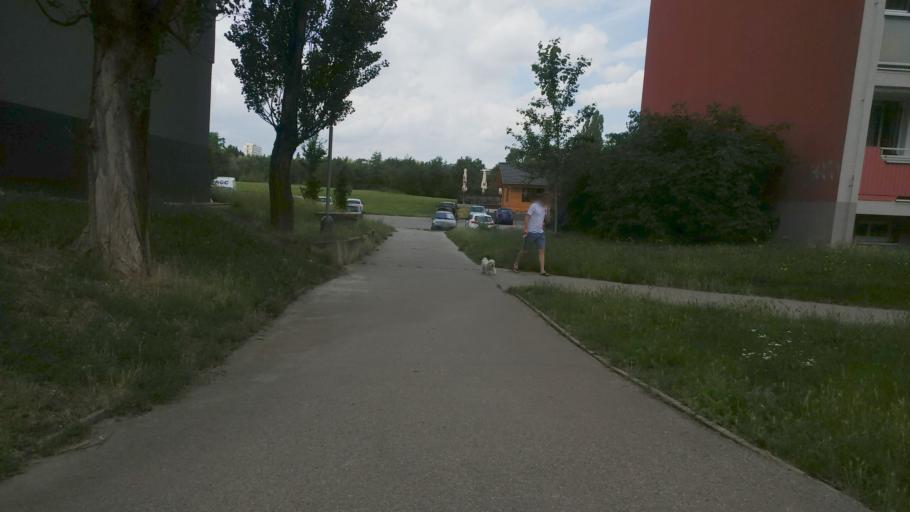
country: CZ
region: Central Bohemia
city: Hostivice
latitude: 50.0463
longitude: 14.3247
